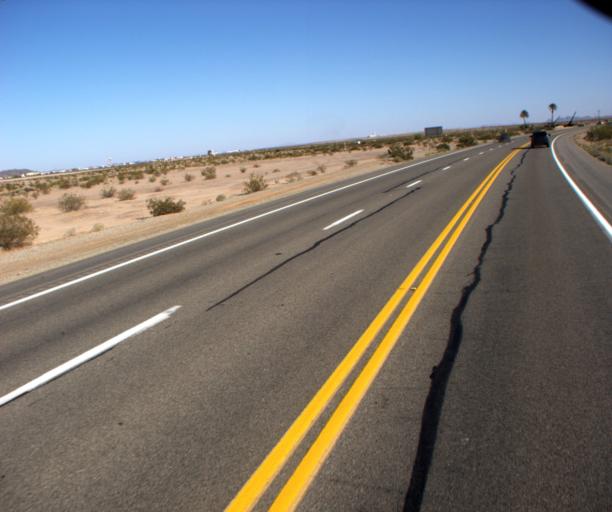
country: US
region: Arizona
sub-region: Yuma County
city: Fortuna Foothills
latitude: 32.8190
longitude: -114.3788
